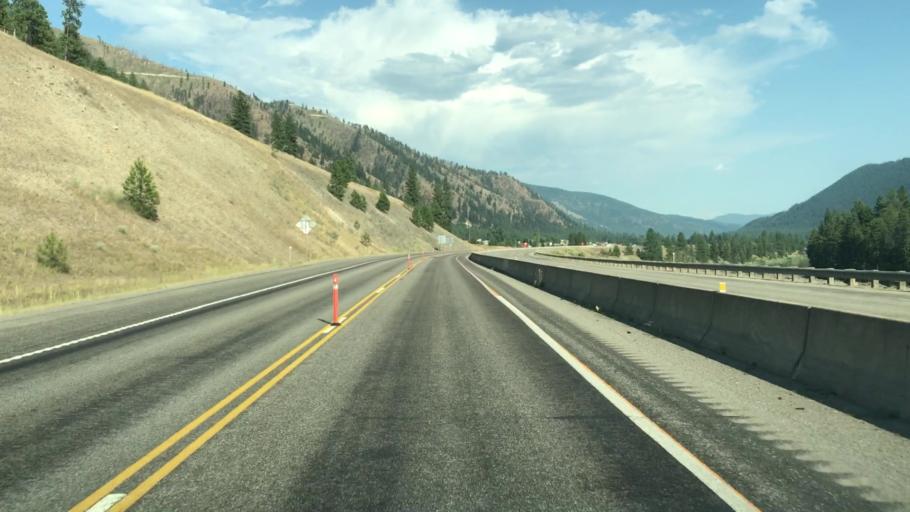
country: US
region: Montana
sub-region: Mineral County
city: Superior
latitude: 47.2168
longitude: -114.9513
